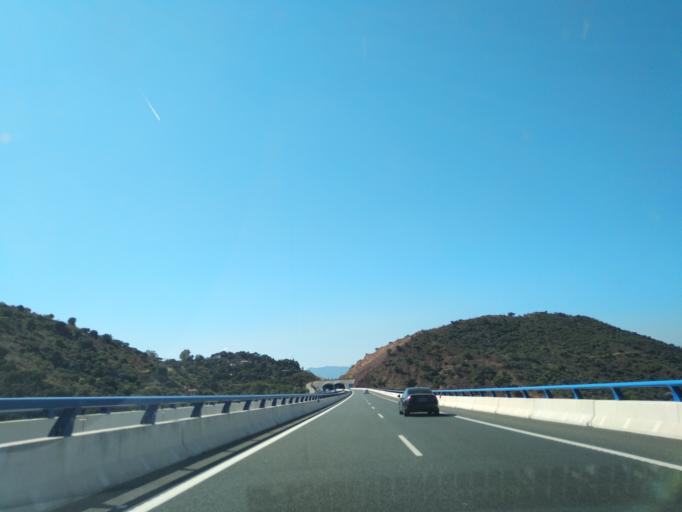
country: ES
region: Andalusia
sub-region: Provincia de Malaga
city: Almogia
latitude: 36.7876
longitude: -4.4715
